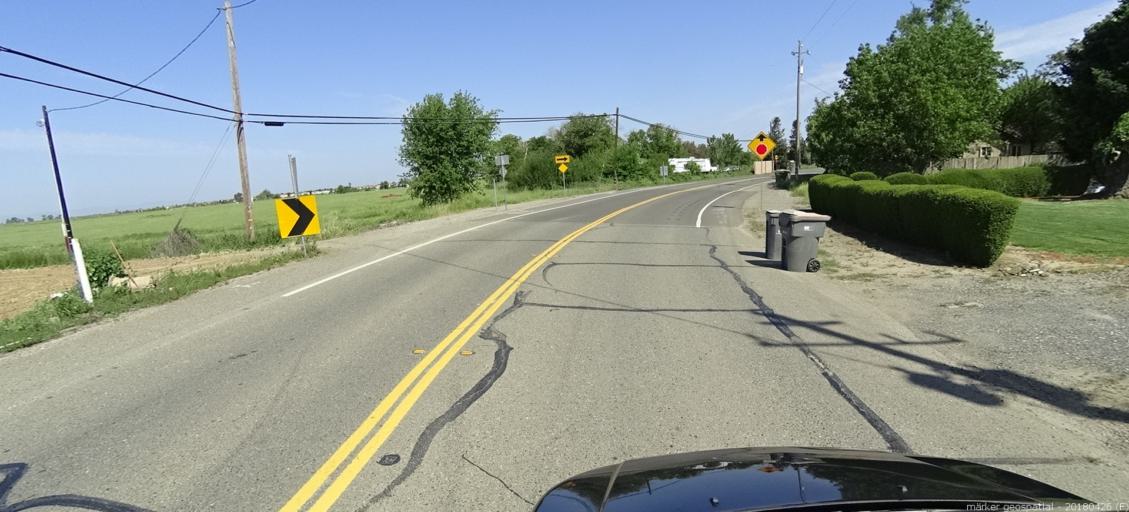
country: US
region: California
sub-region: Yolo County
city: West Sacramento
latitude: 38.5191
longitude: -121.5558
